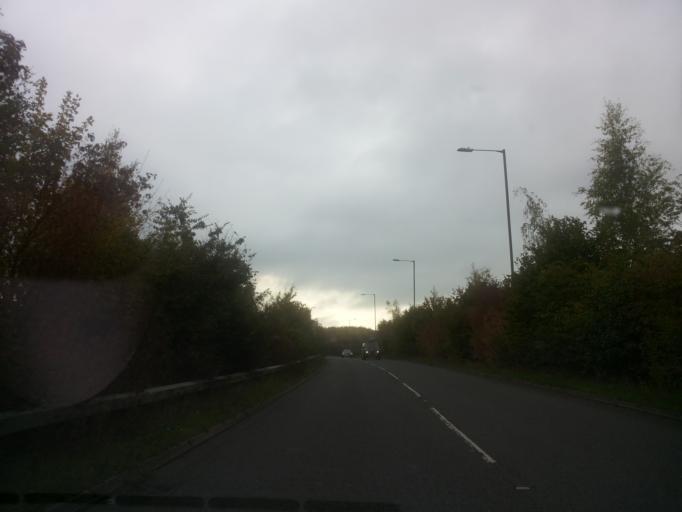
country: GB
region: England
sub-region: Buckinghamshire
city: Wendover
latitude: 51.7553
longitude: -0.7384
